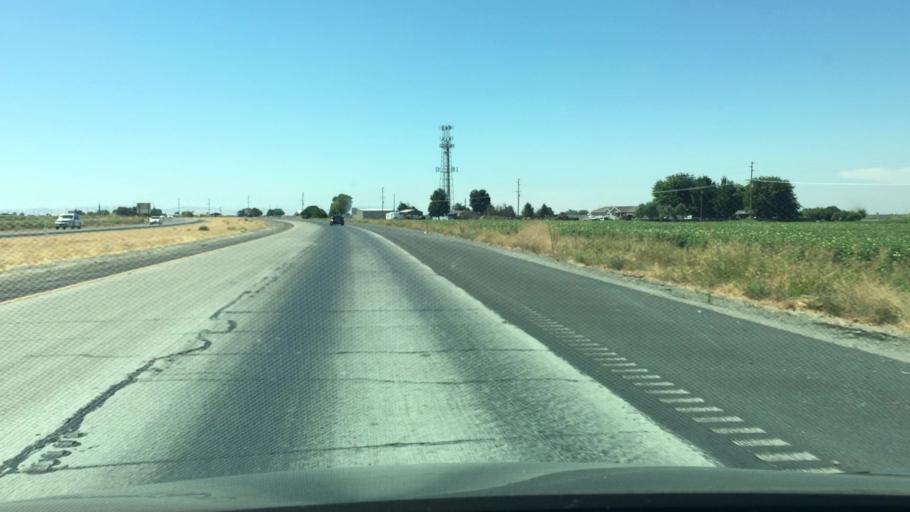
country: US
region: California
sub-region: Merced County
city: Dos Palos
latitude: 37.0530
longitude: -120.6428
